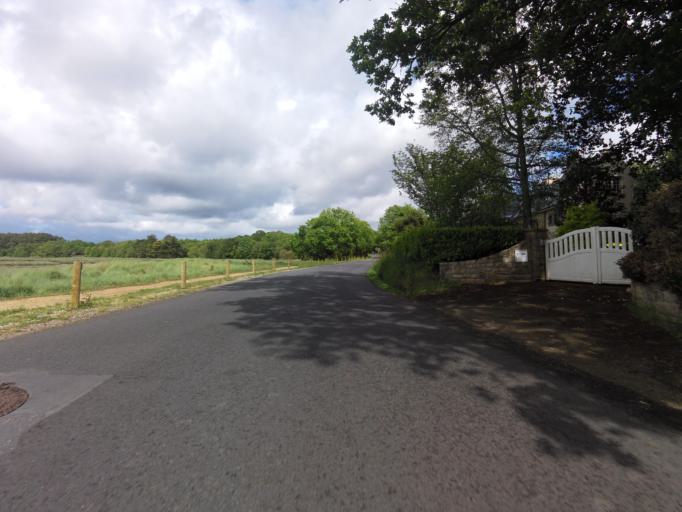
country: FR
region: Brittany
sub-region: Departement du Morbihan
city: Plougoumelen
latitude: 47.6496
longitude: -2.9281
